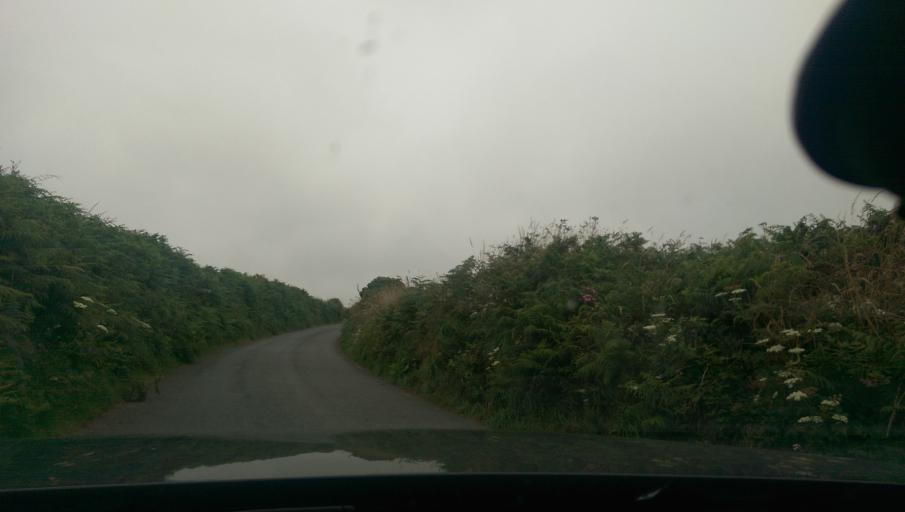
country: GB
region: England
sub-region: Cornwall
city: St. Buryan
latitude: 50.0963
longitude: -5.6498
